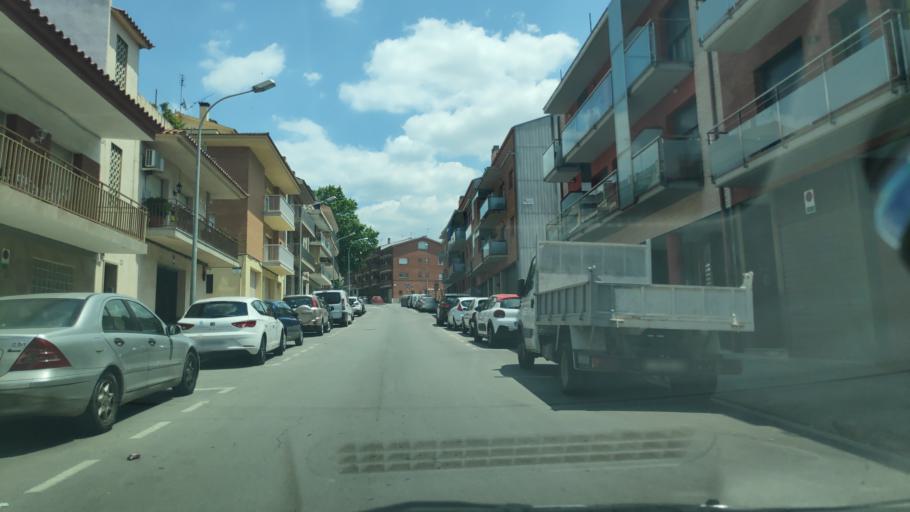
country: ES
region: Catalonia
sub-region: Provincia de Barcelona
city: Les Franqueses del Valles
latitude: 41.6187
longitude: 2.2988
